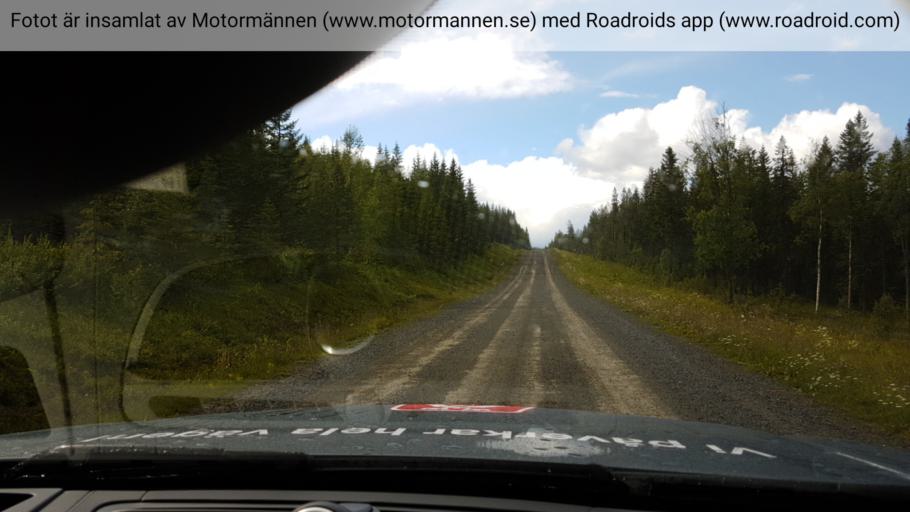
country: SE
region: Jaemtland
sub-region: Bergs Kommun
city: Hoverberg
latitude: 63.0069
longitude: 14.1249
